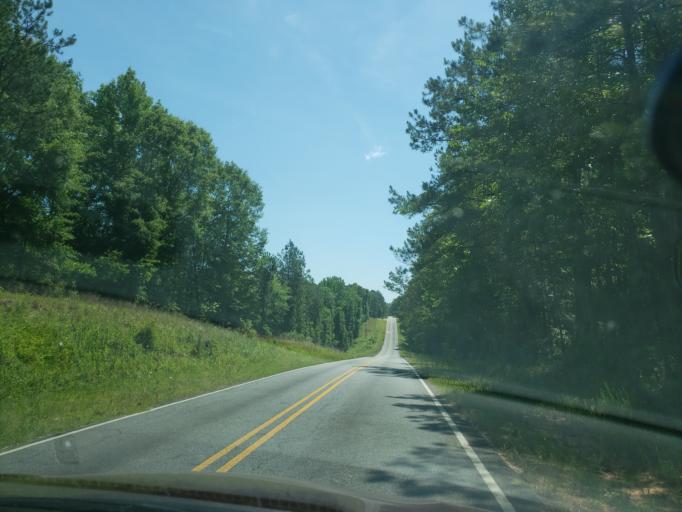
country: US
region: Alabama
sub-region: Elmore County
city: Tallassee
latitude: 32.5808
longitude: -85.8315
